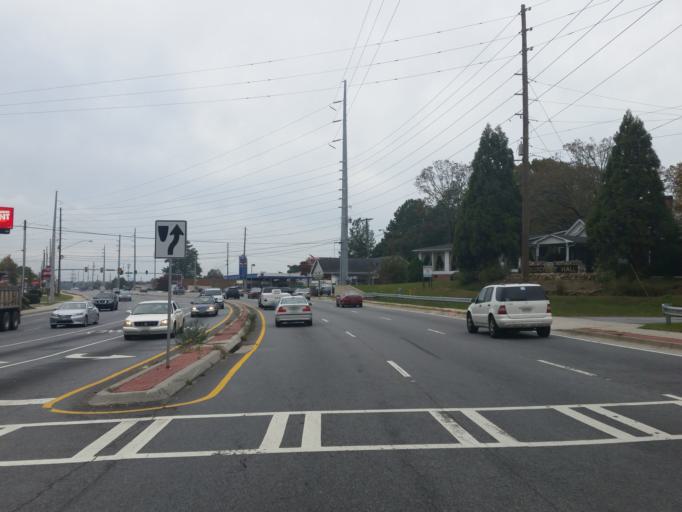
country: US
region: Georgia
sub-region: Cobb County
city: Marietta
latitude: 33.9732
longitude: -84.4859
